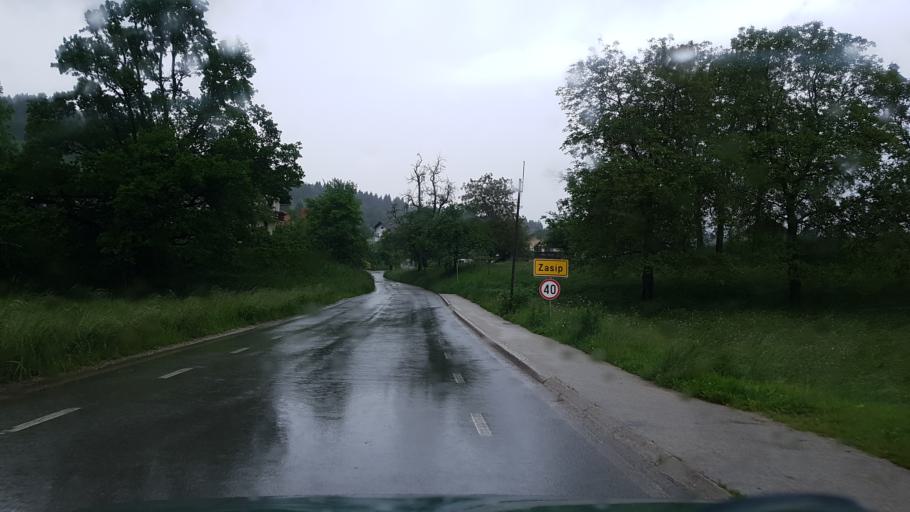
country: SI
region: Bled
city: Zasip
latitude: 46.3856
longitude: 14.1086
